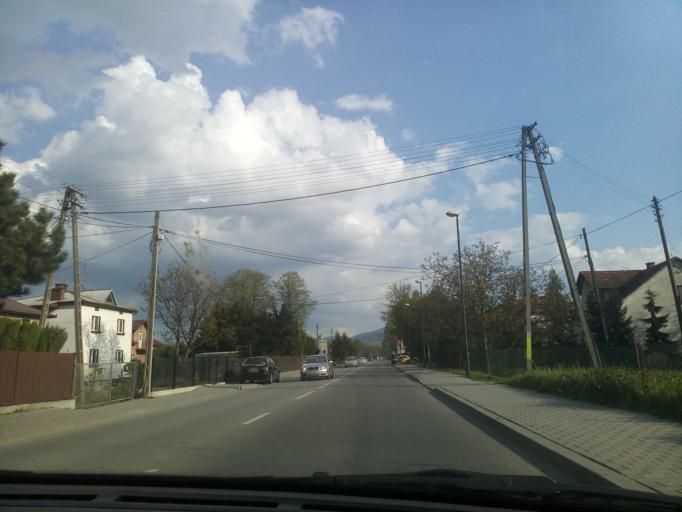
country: PL
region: Lesser Poland Voivodeship
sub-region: Powiat nowosadecki
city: Nawojowa
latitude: 49.5723
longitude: 20.7350
